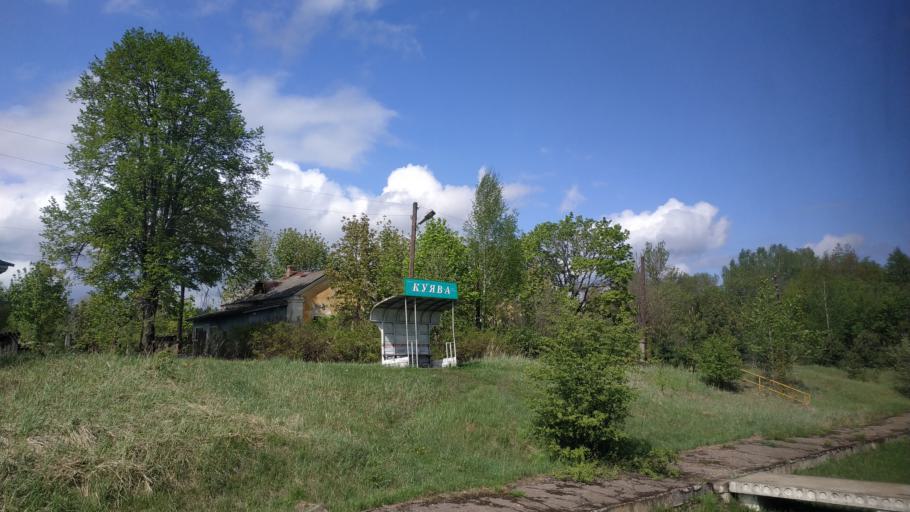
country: RU
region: Kaluga
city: Lyudinovo
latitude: 53.7506
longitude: 34.4079
